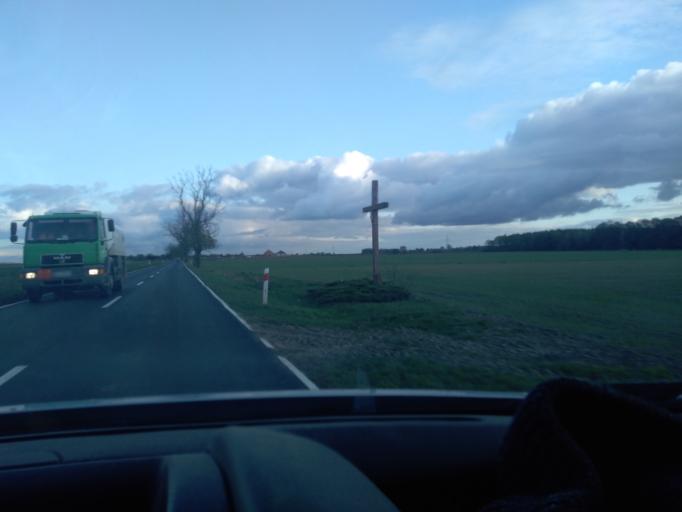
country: PL
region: Greater Poland Voivodeship
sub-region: Powiat poznanski
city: Murowana Goslina
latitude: 52.6339
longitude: 16.9573
